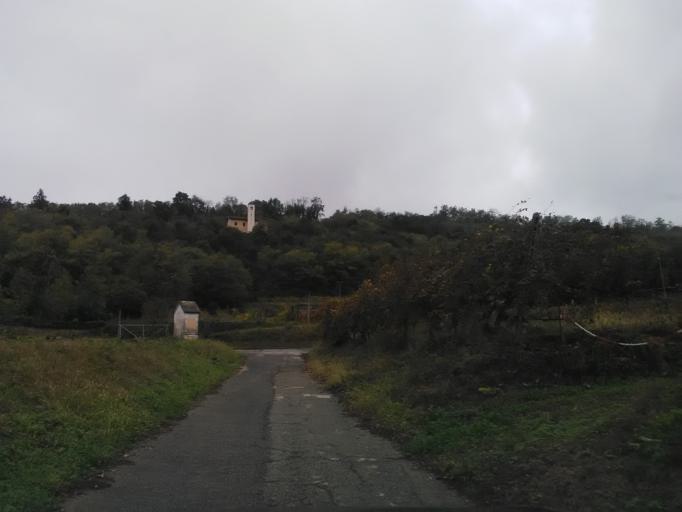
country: IT
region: Piedmont
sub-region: Provincia di Torino
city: Villareggia
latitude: 45.3142
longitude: 7.9766
